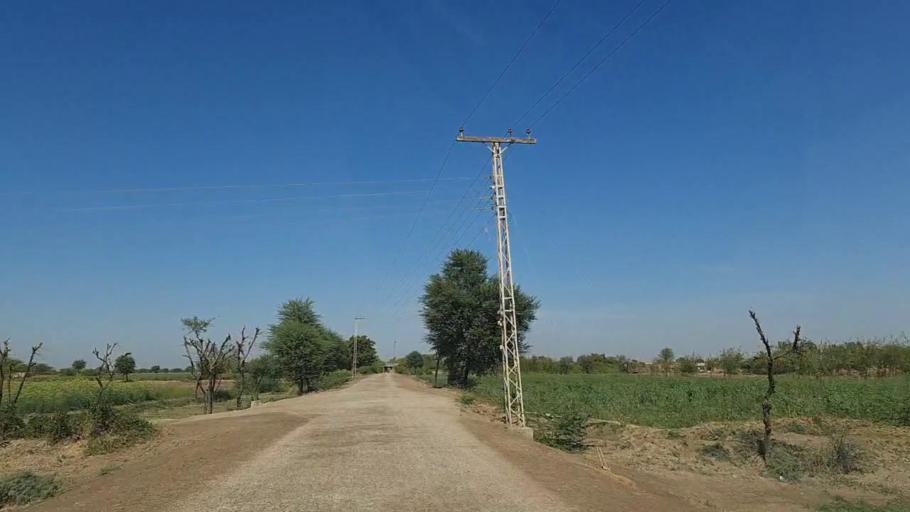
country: PK
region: Sindh
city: Samaro
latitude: 25.3053
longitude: 69.5019
